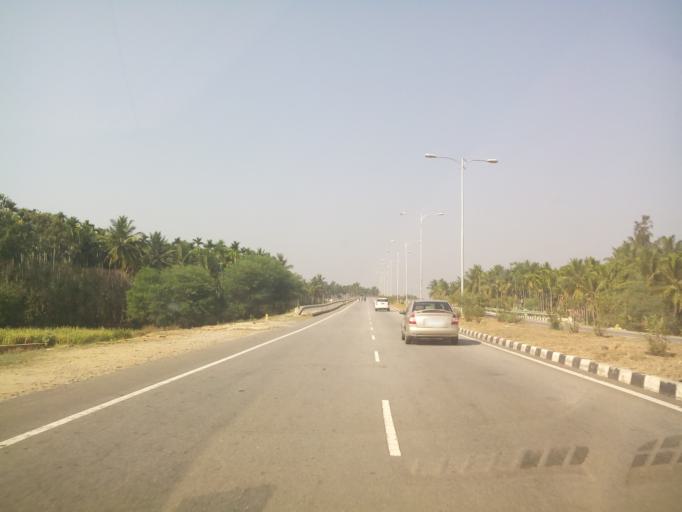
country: IN
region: Karnataka
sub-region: Tumkur
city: Kunigal
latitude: 13.0035
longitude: 77.0274
